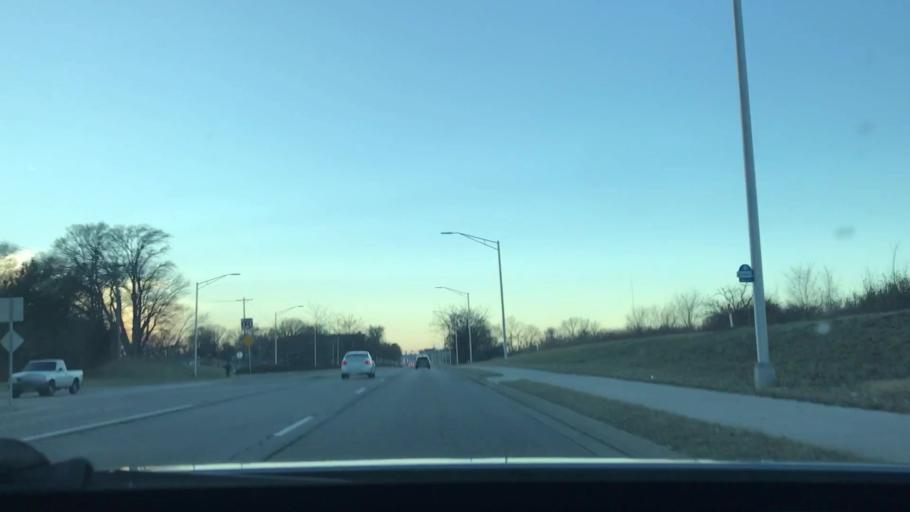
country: US
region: Kansas
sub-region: Wyandotte County
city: Edwardsville
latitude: 39.1165
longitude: -94.7921
